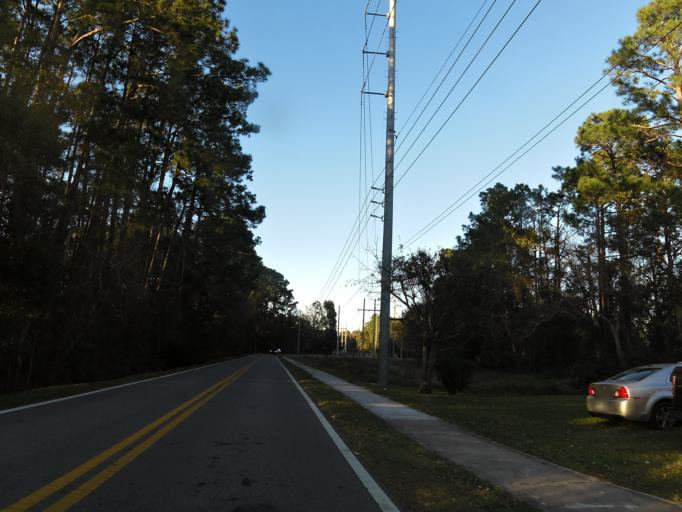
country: US
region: Florida
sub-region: Saint Johns County
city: Fruit Cove
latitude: 30.1826
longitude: -81.6122
